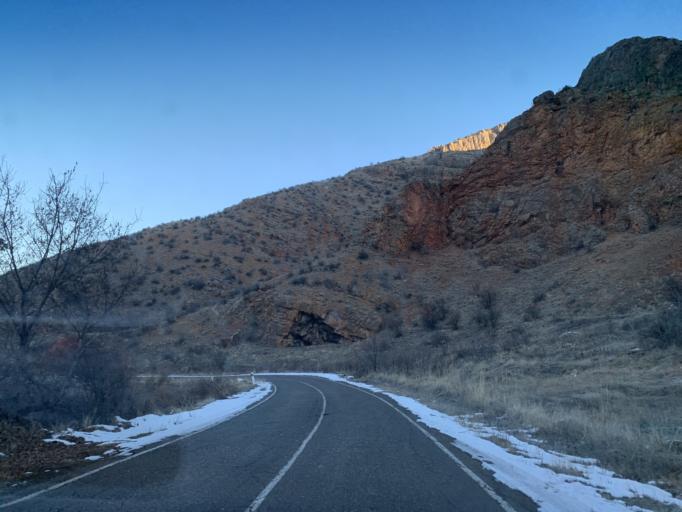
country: AM
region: Vayots' Dzori Marz
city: Areni
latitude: 39.6901
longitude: 45.2204
